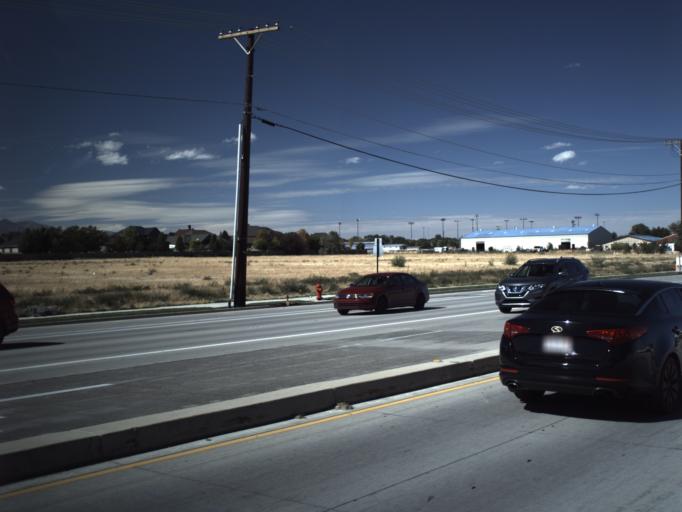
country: US
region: Utah
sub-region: Salt Lake County
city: South Jordan
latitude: 40.5451
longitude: -111.9386
